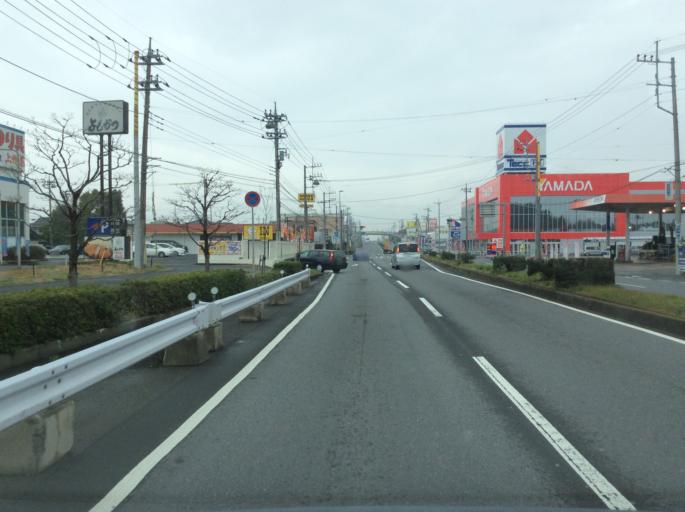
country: JP
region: Ibaraki
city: Mitsukaido
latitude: 35.9767
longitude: 139.9828
